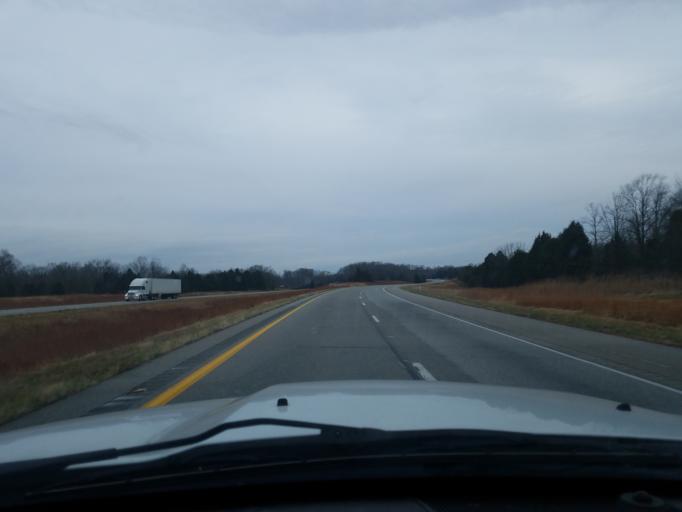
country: US
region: Indiana
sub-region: Harrison County
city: Corydon
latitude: 38.2507
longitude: -86.2727
